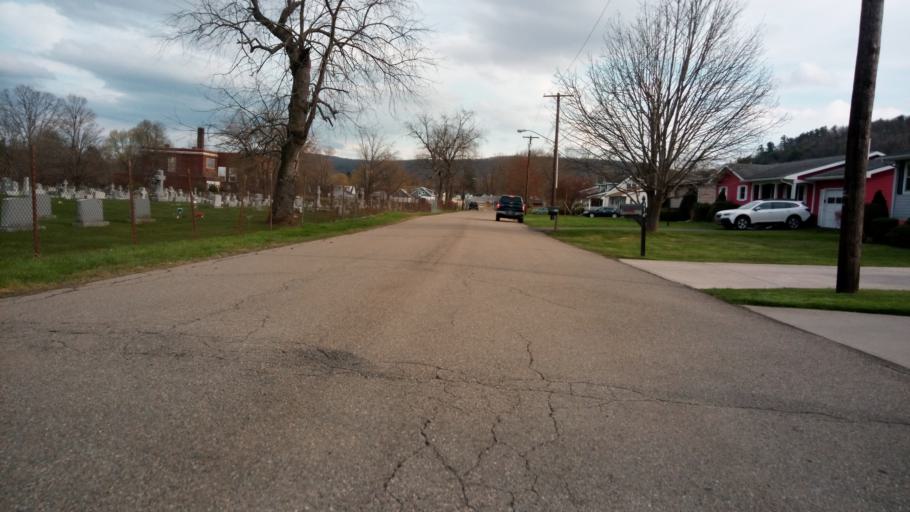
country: US
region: New York
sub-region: Chemung County
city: Southport
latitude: 42.0717
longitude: -76.8212
